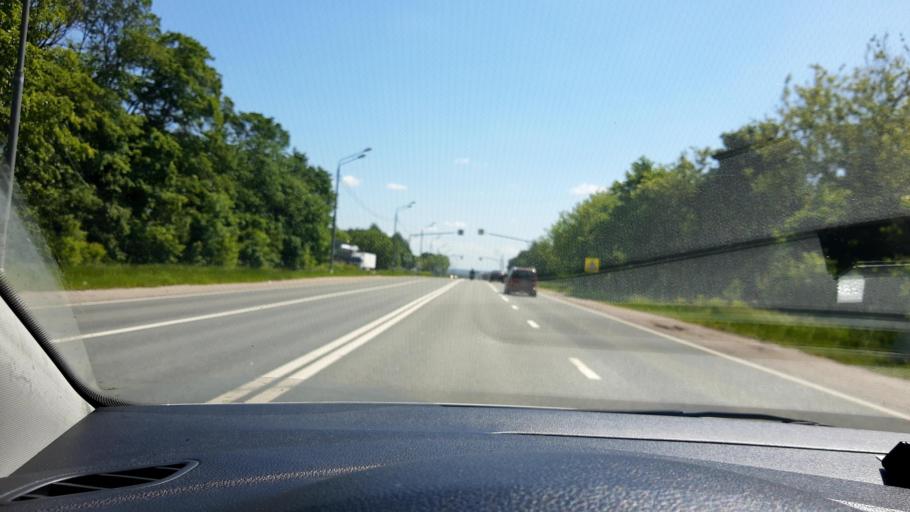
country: RU
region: Moskovskaya
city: Bronnitsy
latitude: 55.4760
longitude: 38.1859
